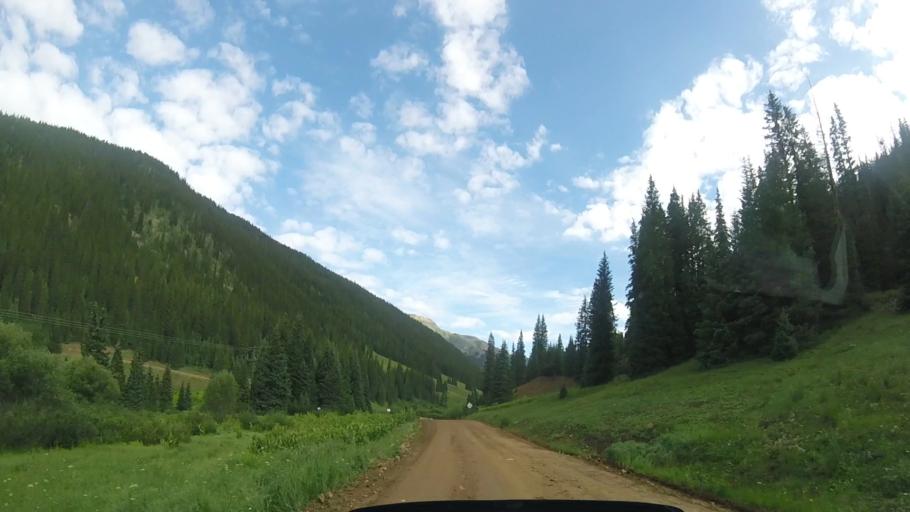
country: US
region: Colorado
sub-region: San Juan County
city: Silverton
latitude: 37.8493
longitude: -107.7256
